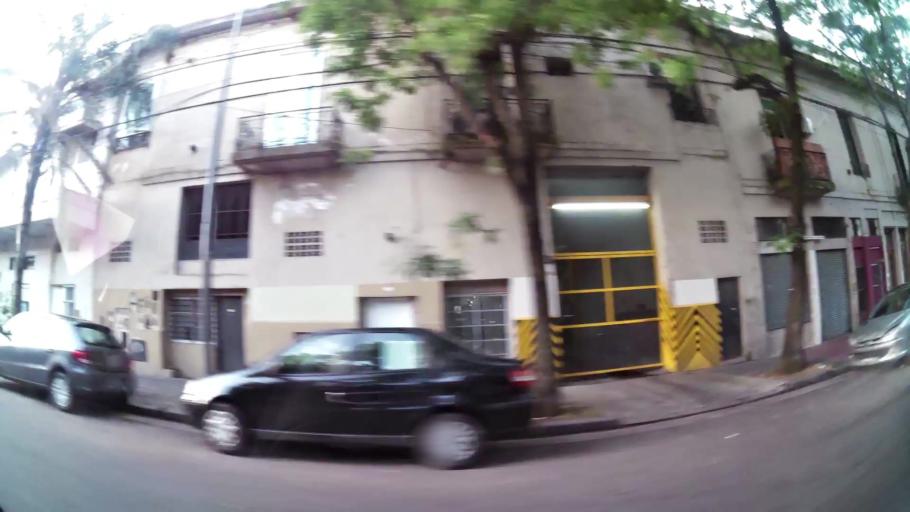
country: AR
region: Buenos Aires F.D.
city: Buenos Aires
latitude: -34.6334
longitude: -58.4134
